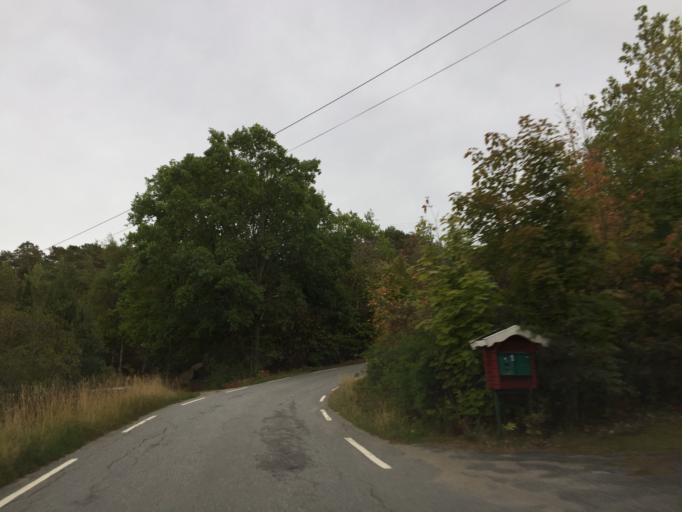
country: NO
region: Ostfold
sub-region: Hvaler
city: Skjaerhalden
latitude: 59.0565
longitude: 11.0053
